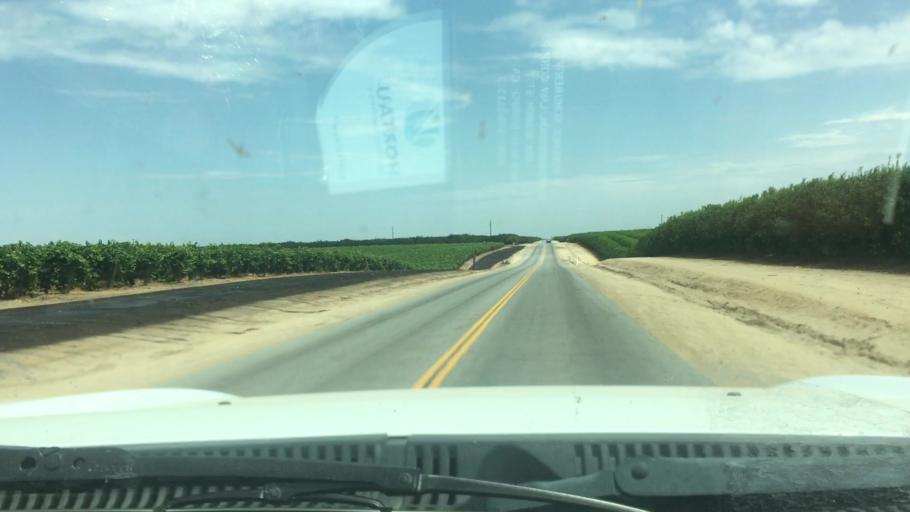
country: US
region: California
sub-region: Kern County
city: McFarland
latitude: 35.5697
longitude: -119.1511
